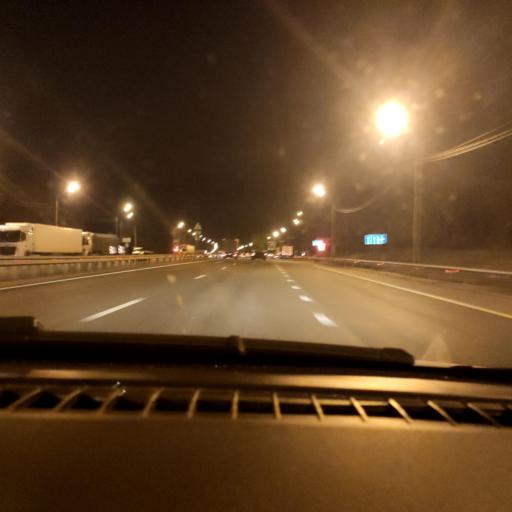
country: RU
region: Lipetsk
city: Khlevnoye
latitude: 52.1318
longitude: 39.1985
